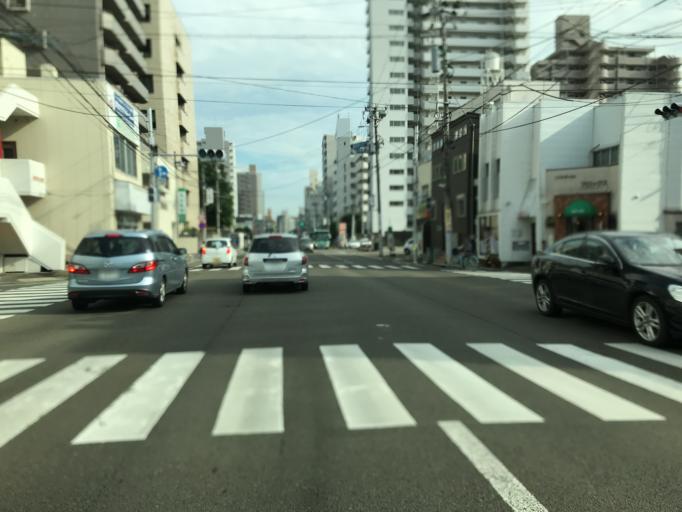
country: JP
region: Miyagi
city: Sendai-shi
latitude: 38.2701
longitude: 140.8620
